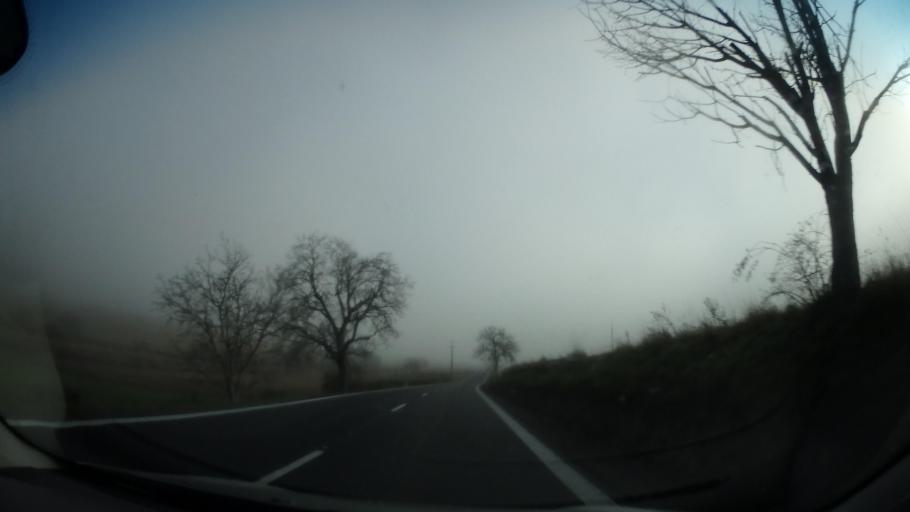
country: CZ
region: South Moravian
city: Zdanice
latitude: 49.0423
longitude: 17.0115
